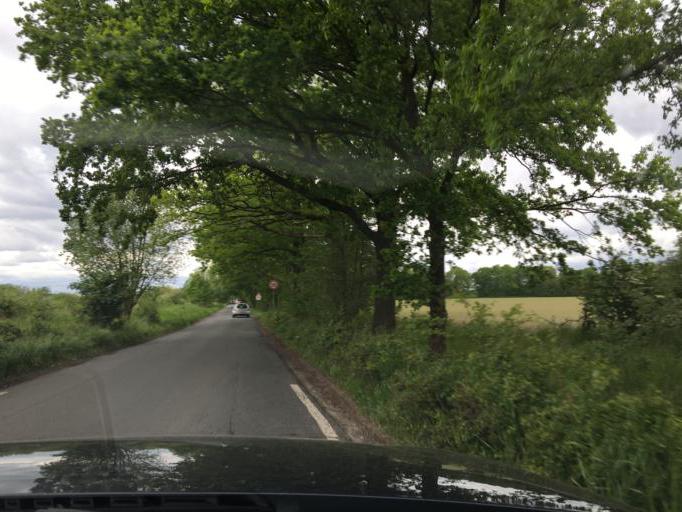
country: DE
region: North Rhine-Westphalia
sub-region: Regierungsbezirk Munster
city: Muenster
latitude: 52.0232
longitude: 7.6636
